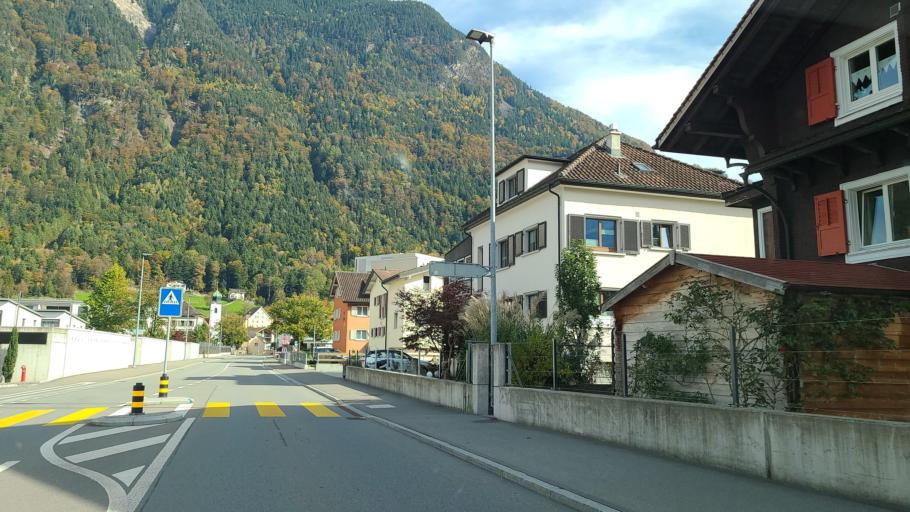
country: CH
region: Uri
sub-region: Uri
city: Altdorf
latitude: 46.8818
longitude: 8.6348
